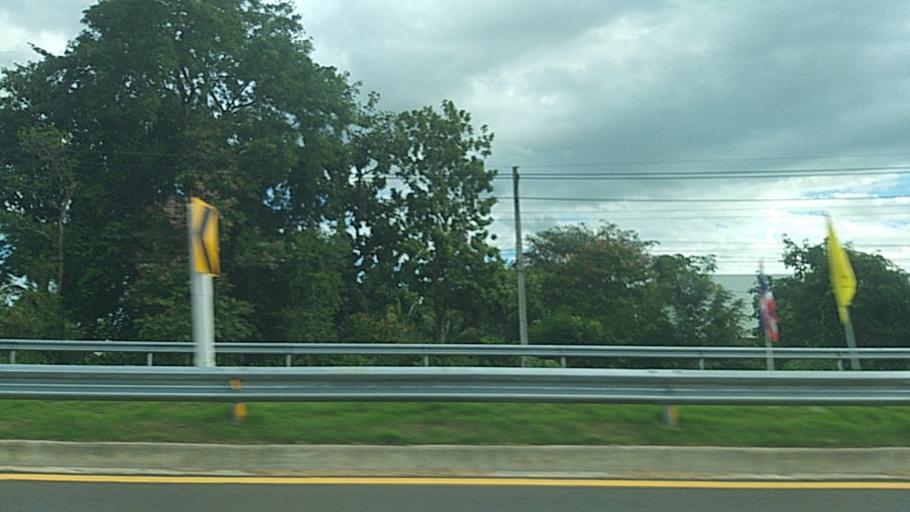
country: TH
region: Surin
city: Prasat
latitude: 14.5921
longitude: 103.4484
